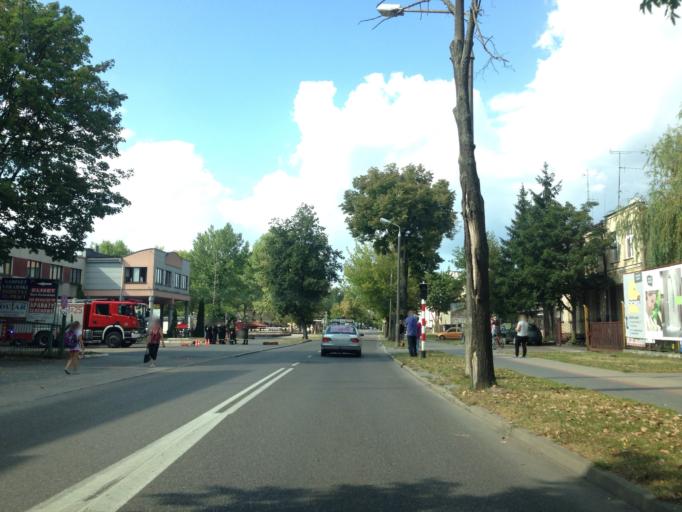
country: PL
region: Warmian-Masurian Voivodeship
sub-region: Powiat ilawski
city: Ilawa
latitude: 53.5888
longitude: 19.5711
